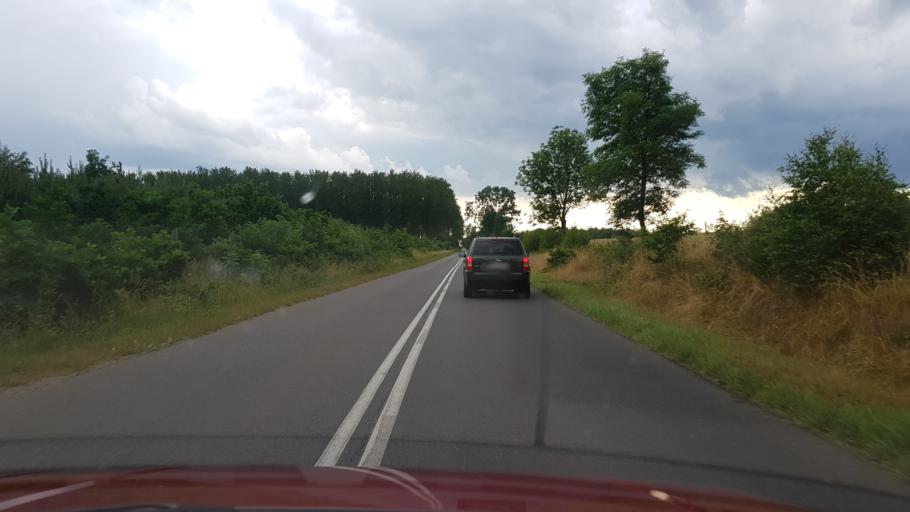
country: PL
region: West Pomeranian Voivodeship
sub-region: Powiat gryficki
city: Gryfice
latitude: 53.8828
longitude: 15.1518
